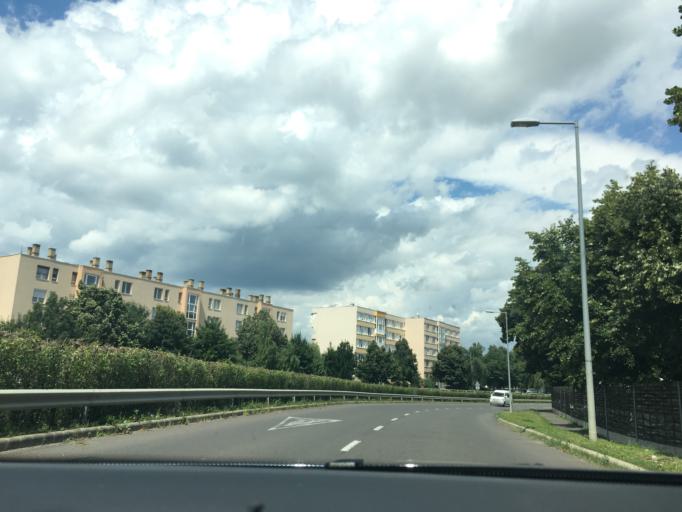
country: HU
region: Borsod-Abauj-Zemplen
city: Satoraljaujhely
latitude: 48.3980
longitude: 21.6622
